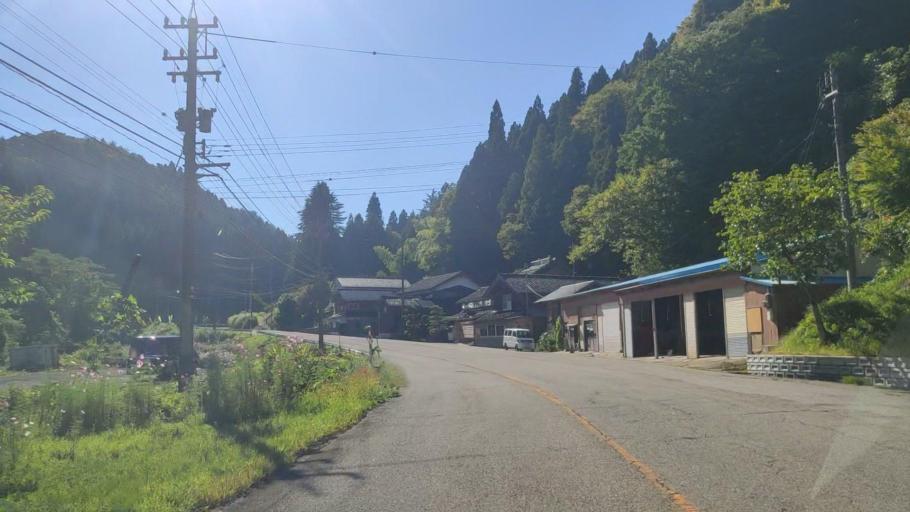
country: JP
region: Ishikawa
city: Nanao
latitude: 37.3276
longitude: 137.2019
